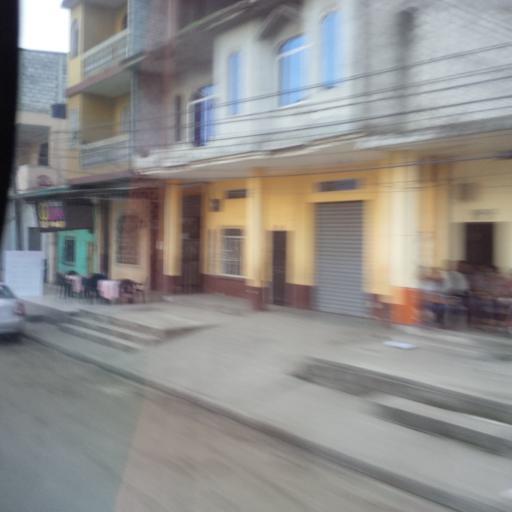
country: EC
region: Canar
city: La Troncal
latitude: -2.3335
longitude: -79.4008
